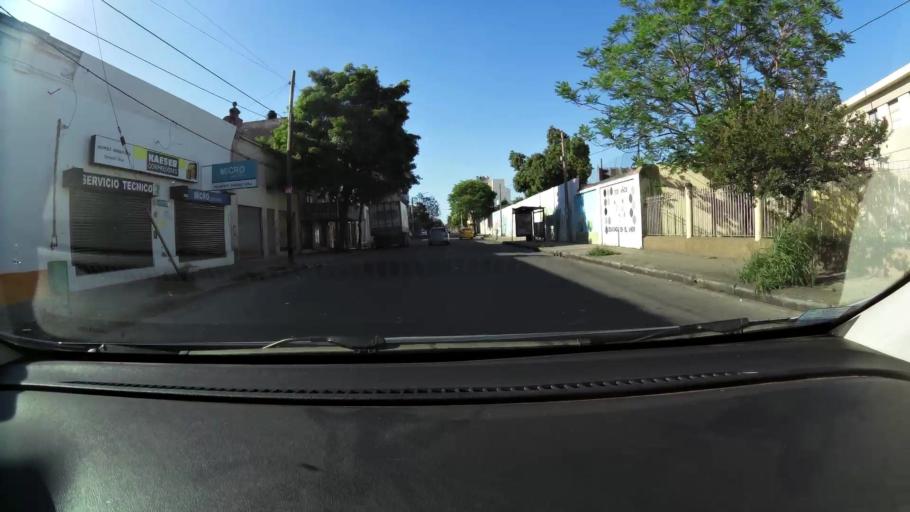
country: AR
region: Cordoba
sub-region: Departamento de Capital
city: Cordoba
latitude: -31.3950
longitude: -64.1759
